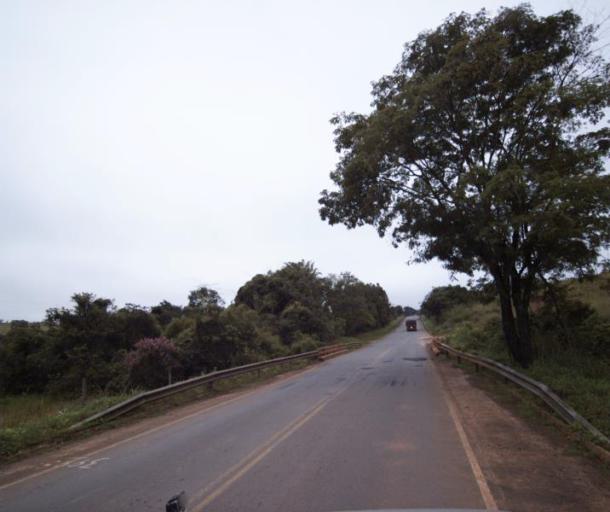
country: BR
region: Goias
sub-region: Pirenopolis
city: Pirenopolis
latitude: -15.9820
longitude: -48.8281
